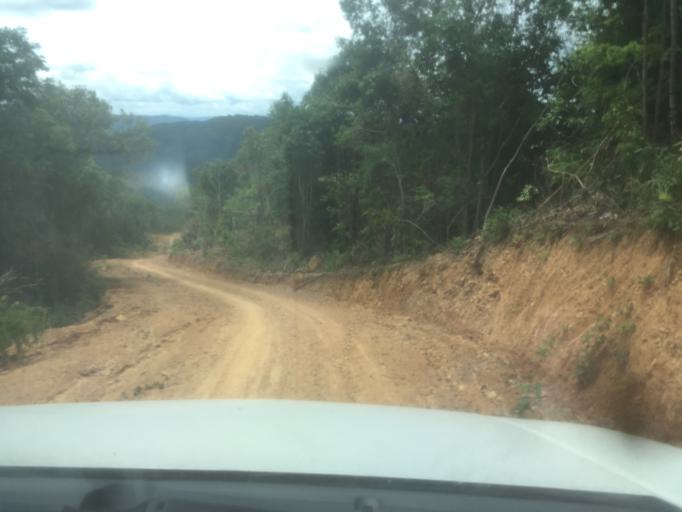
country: LA
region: Phongsali
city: Khoa
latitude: 20.9246
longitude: 102.5522
